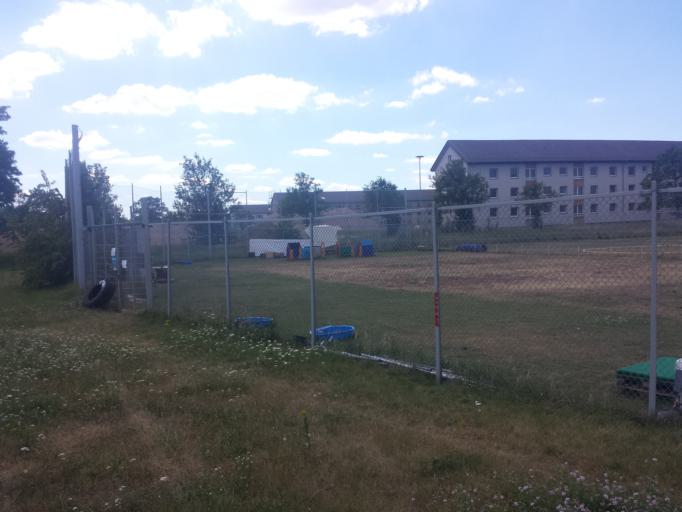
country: DE
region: Hesse
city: Viernheim
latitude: 49.5177
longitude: 8.5318
